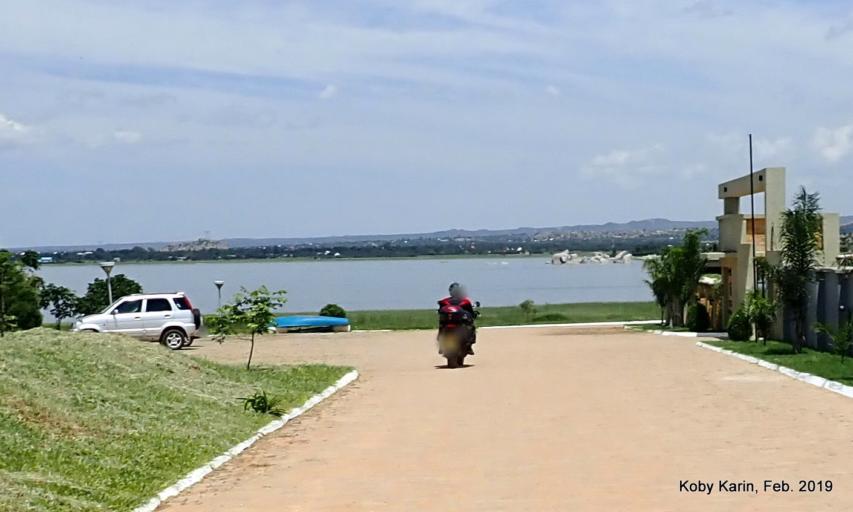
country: TZ
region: Singida
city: Singida
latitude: -4.7948
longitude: 34.7403
